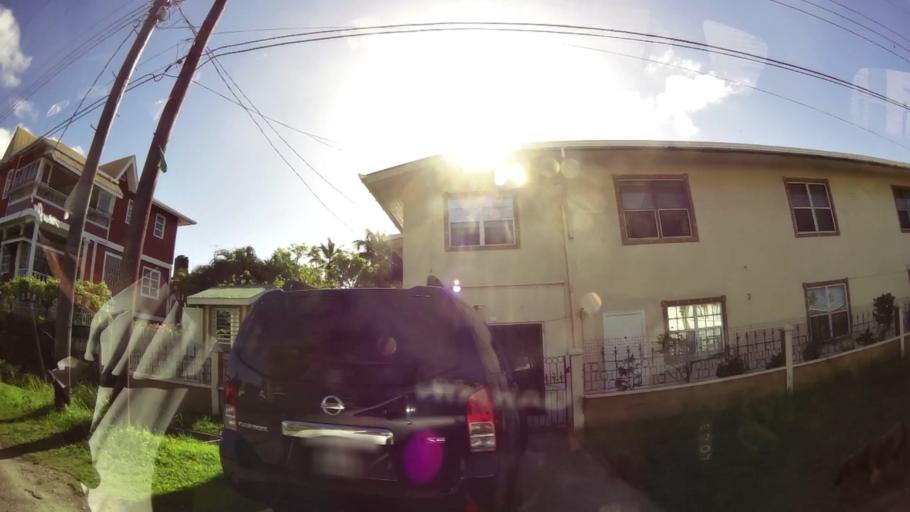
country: GY
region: Demerara-Mahaica
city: Georgetown
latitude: 6.8224
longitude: -58.1359
